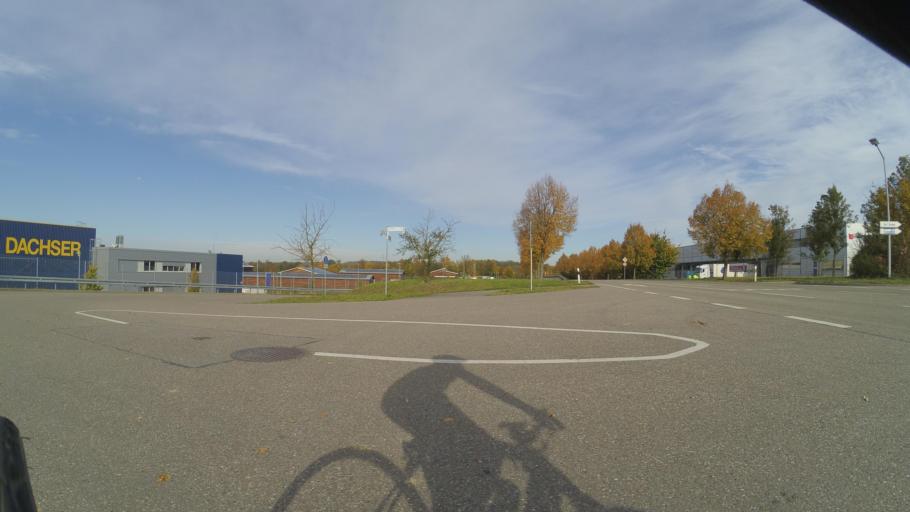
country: DE
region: Baden-Wuerttemberg
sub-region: Regierungsbezirk Stuttgart
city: Ohringen
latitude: 49.2019
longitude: 9.4751
